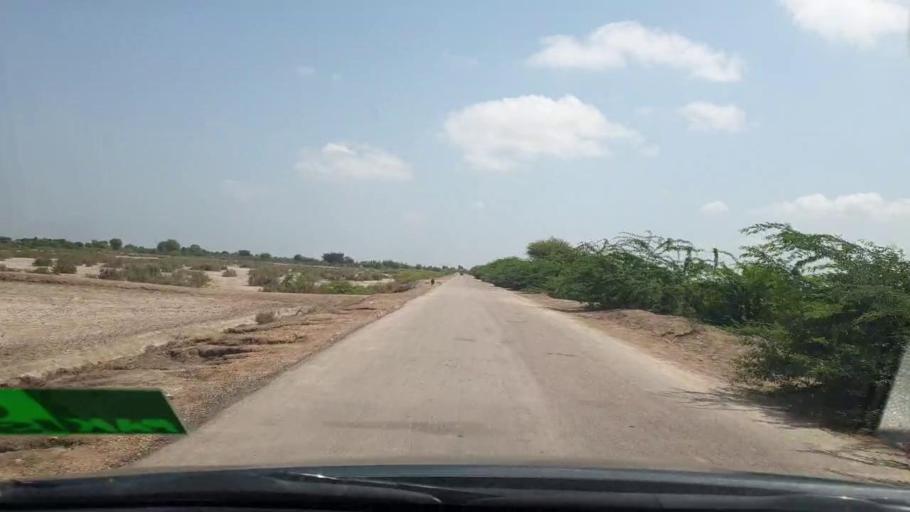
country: PK
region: Sindh
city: Digri
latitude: 25.0011
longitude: 69.1391
